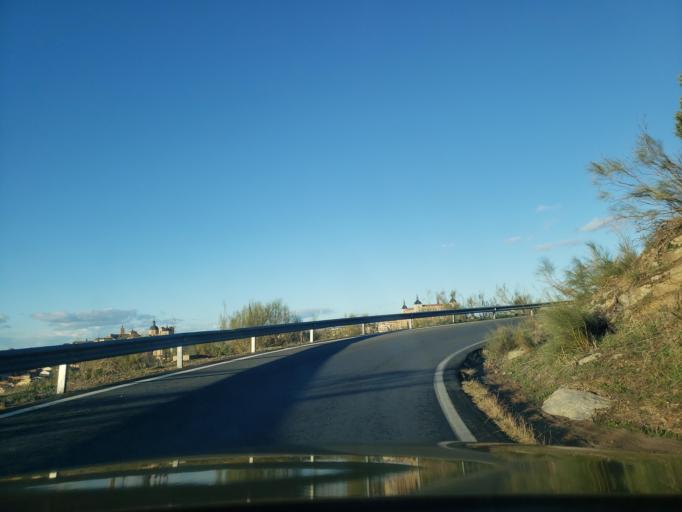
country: ES
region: Castille-La Mancha
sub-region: Province of Toledo
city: Toledo
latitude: 39.8494
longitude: -4.0244
